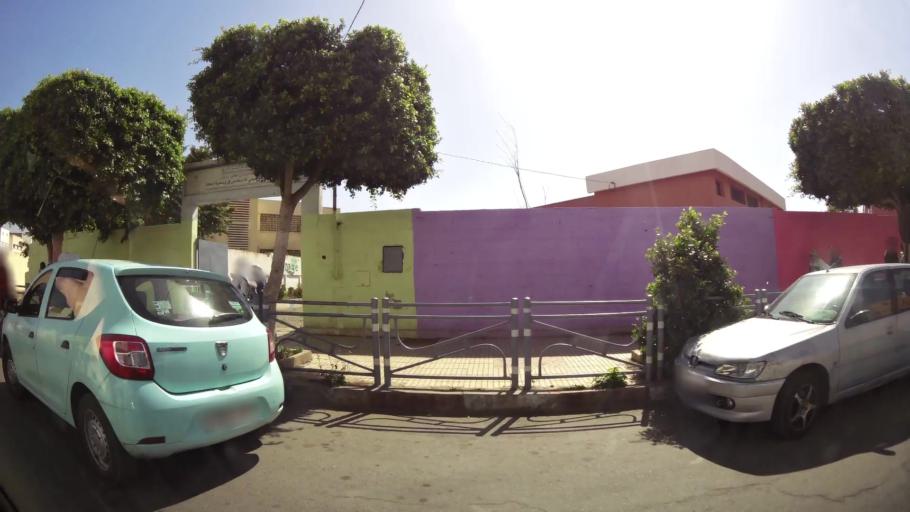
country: MA
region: Souss-Massa-Draa
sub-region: Inezgane-Ait Mellou
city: Inezgane
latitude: 30.3582
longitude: -9.5386
